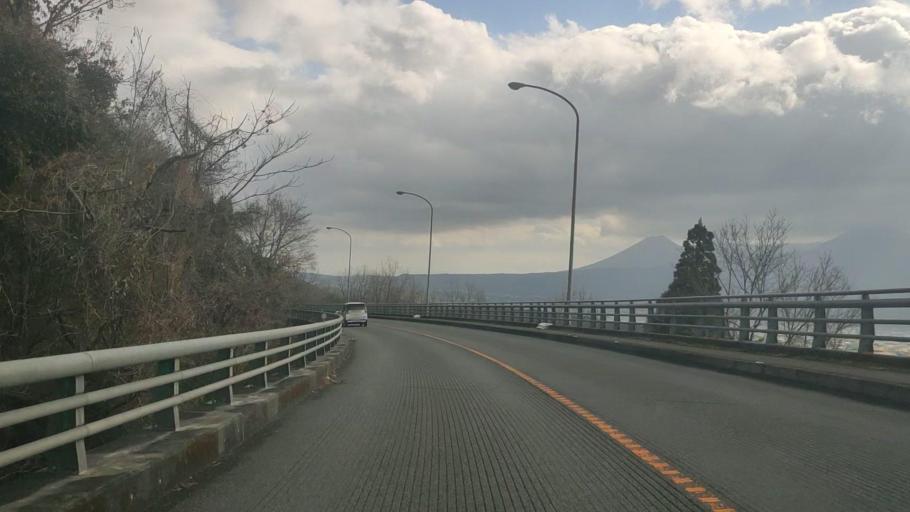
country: JP
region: Kumamoto
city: Hitoyoshi
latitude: 32.0713
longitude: 130.7973
